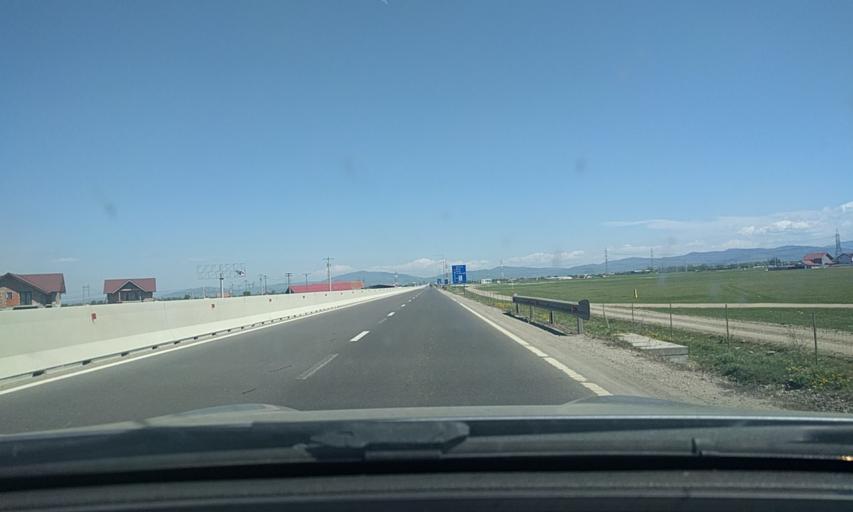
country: RO
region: Brasov
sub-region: Comuna Sanpetru
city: Sanpetru
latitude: 45.6885
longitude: 25.6300
